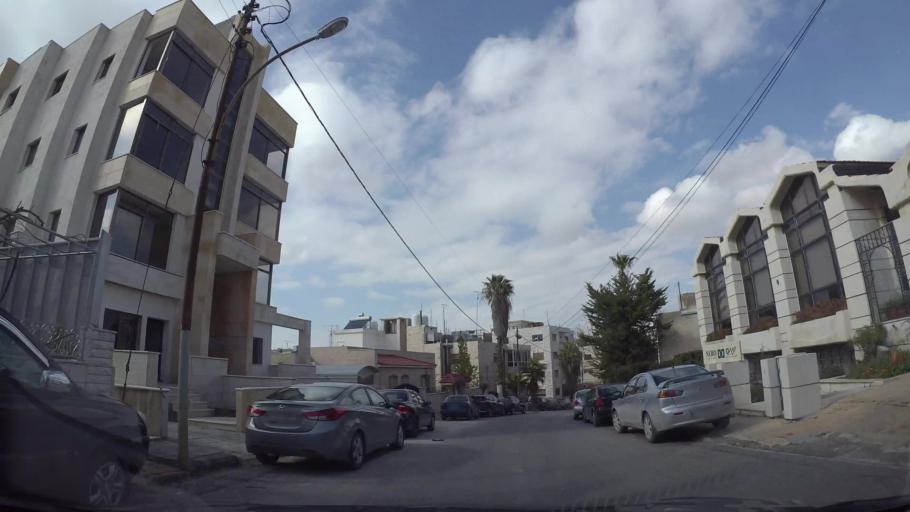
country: JO
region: Amman
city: Amman
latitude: 31.9646
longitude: 35.8898
